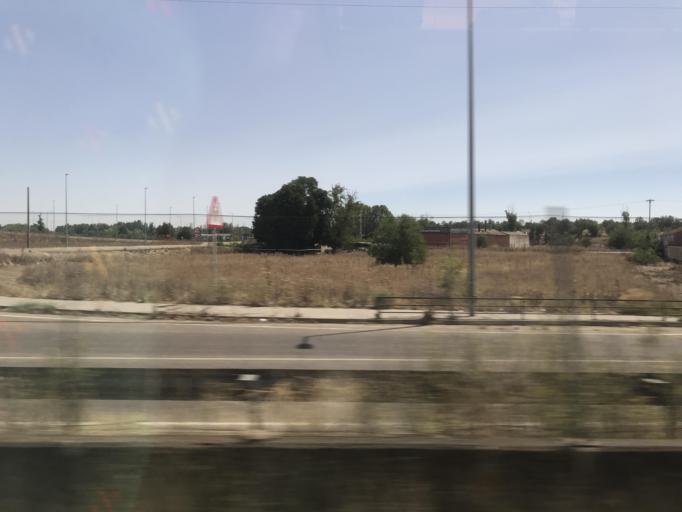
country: ES
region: Castille and Leon
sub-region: Provincia de Valladolid
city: Valladolid
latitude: 41.6632
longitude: -4.7022
